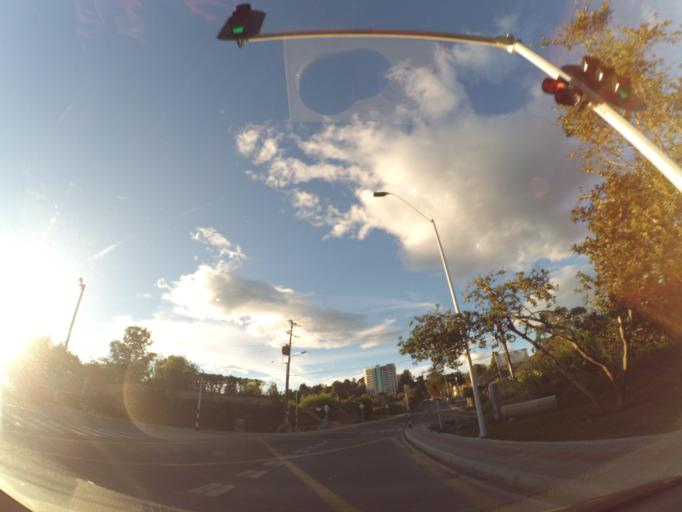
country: CO
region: Cauca
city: Popayan
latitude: 2.4696
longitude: -76.5783
